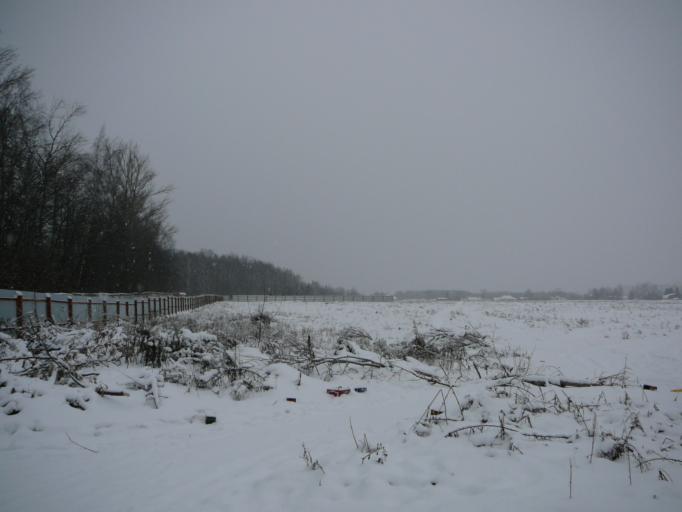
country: RU
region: Moskovskaya
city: Lesnoy Gorodok
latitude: 55.6657
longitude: 37.1828
